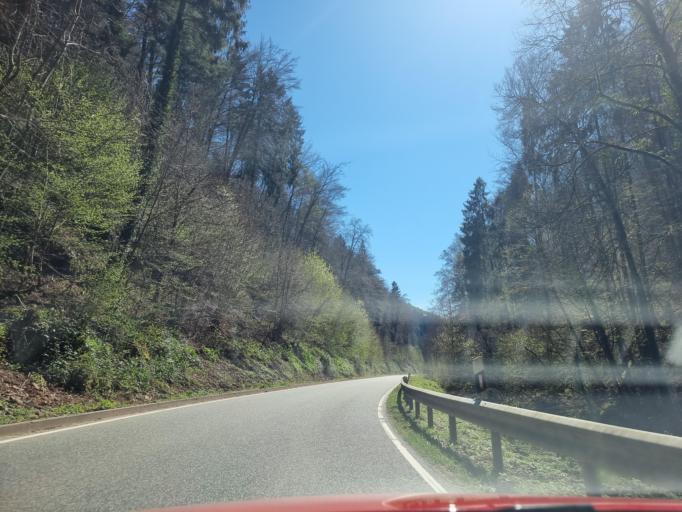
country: DE
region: Rheinland-Pfalz
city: Kordel
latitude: 49.8531
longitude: 6.6196
